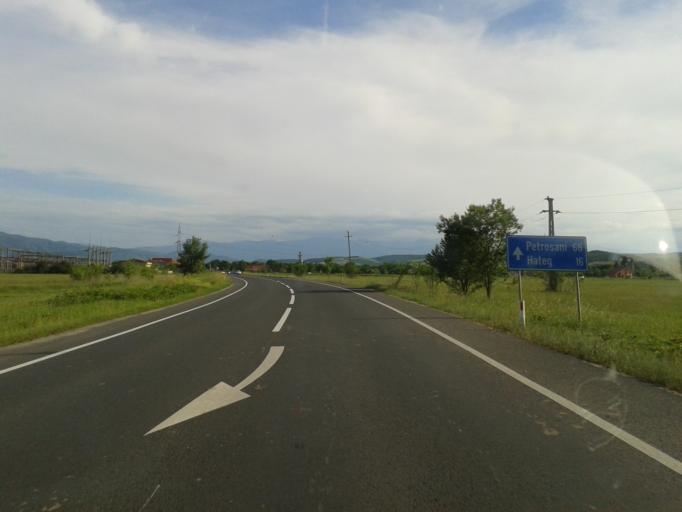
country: RO
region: Hunedoara
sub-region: Comuna Calan
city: Calan
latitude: 45.7227
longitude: 22.9945
